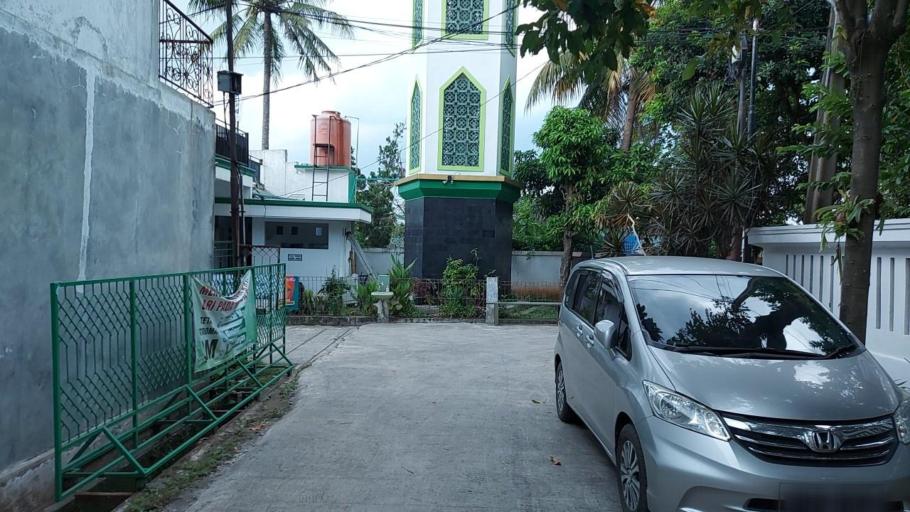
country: ID
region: West Java
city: Citeureup
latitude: -6.4913
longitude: 106.8754
